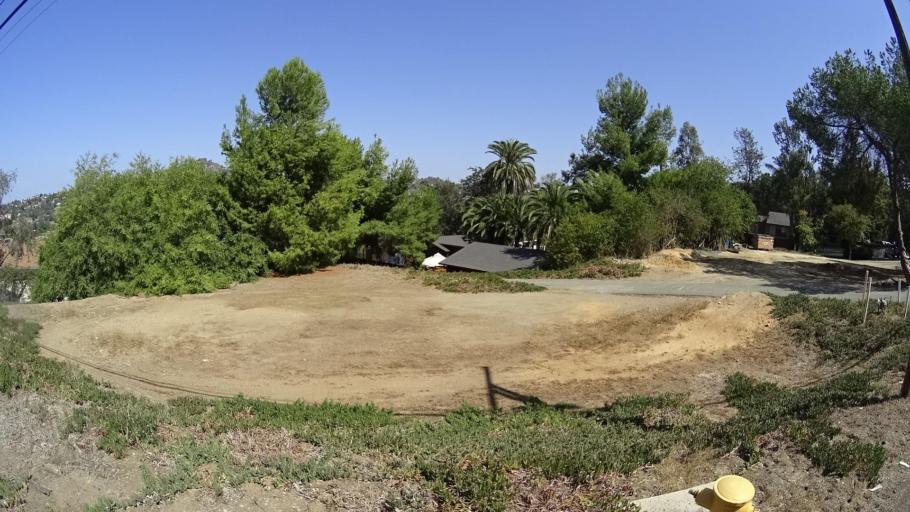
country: US
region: California
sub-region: San Diego County
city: Spring Valley
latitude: 32.7392
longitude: -116.9903
